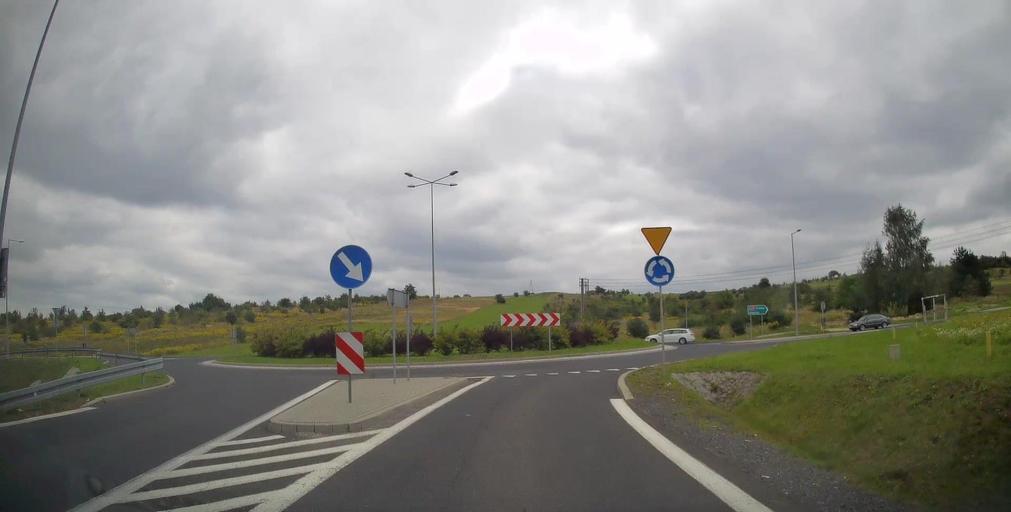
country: PL
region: Lesser Poland Voivodeship
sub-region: Powiat chrzanowski
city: Grojec
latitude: 50.1025
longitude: 19.5554
